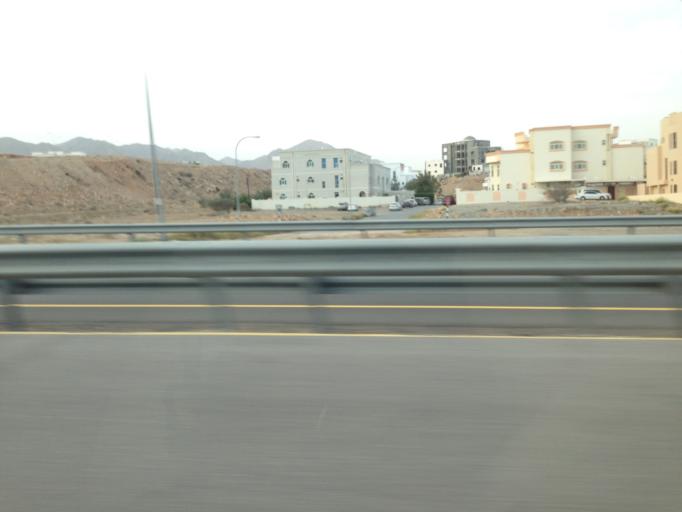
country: OM
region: Muhafazat Masqat
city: Bawshar
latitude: 23.5637
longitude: 58.3869
